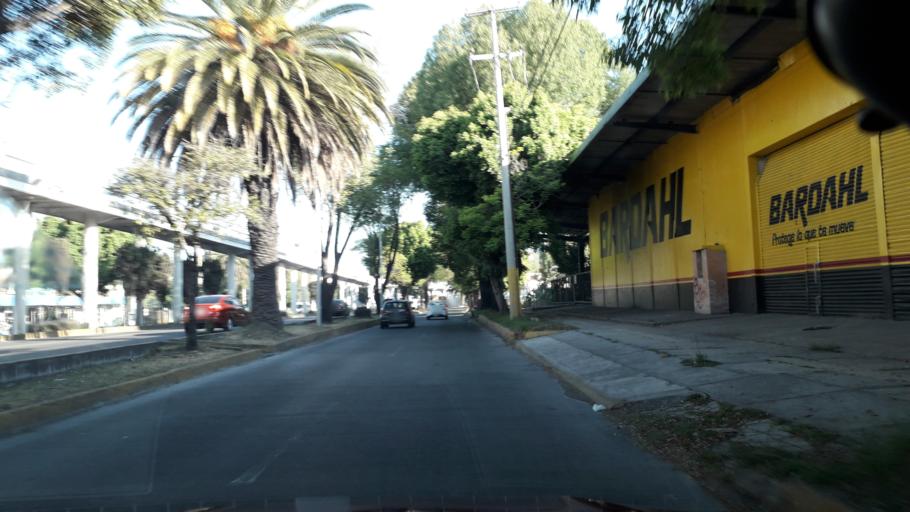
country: MX
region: Puebla
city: Puebla
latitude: 19.0611
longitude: -98.2204
